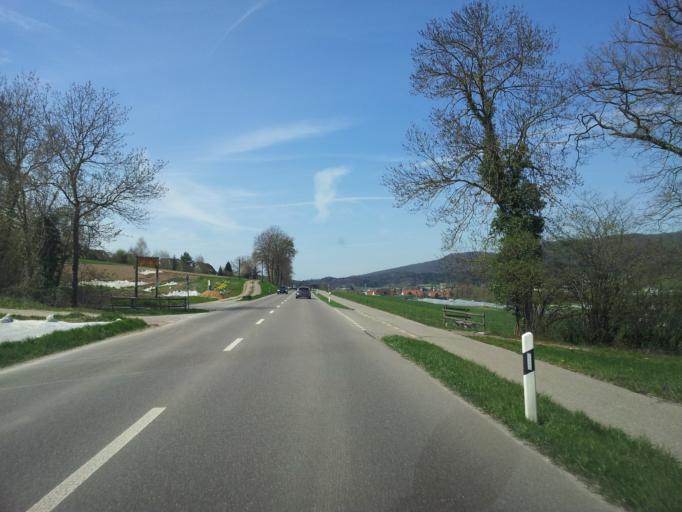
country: CH
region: Zurich
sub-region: Bezirk Dielsdorf
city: Daenikon
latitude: 47.4446
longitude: 8.4169
